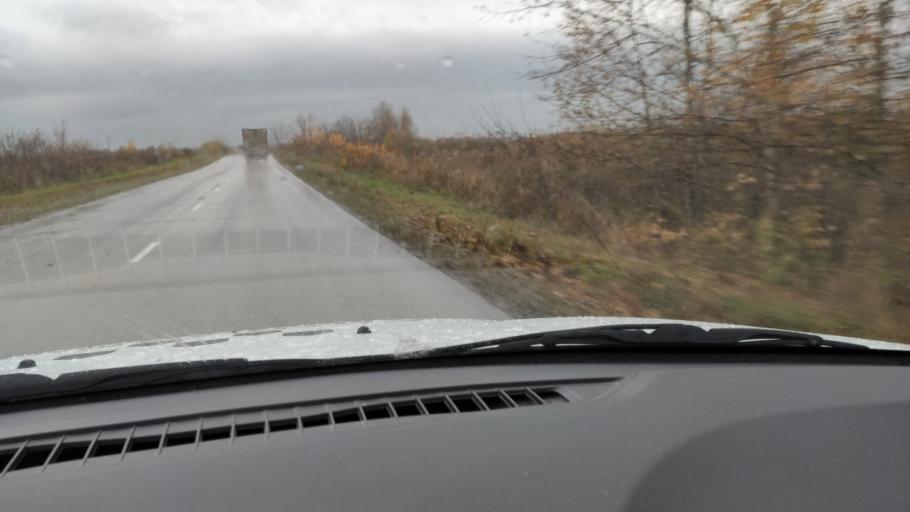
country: RU
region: Perm
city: Kondratovo
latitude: 58.0015
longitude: 56.0683
